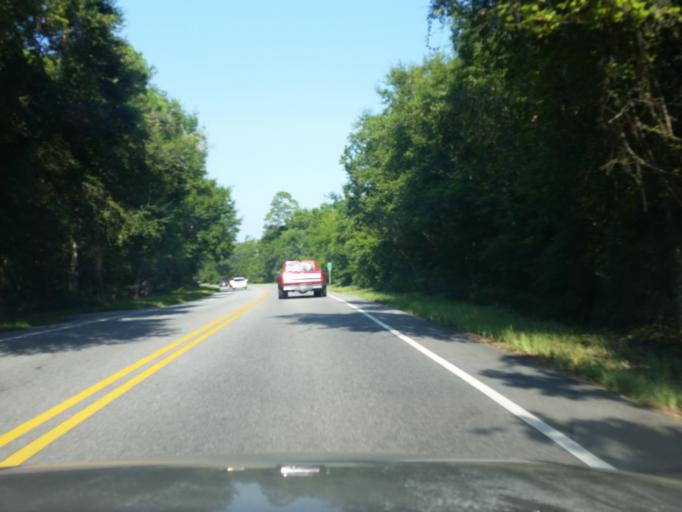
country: US
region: Alabama
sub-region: Baldwin County
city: Gulf Shores
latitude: 30.2480
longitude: -87.8284
